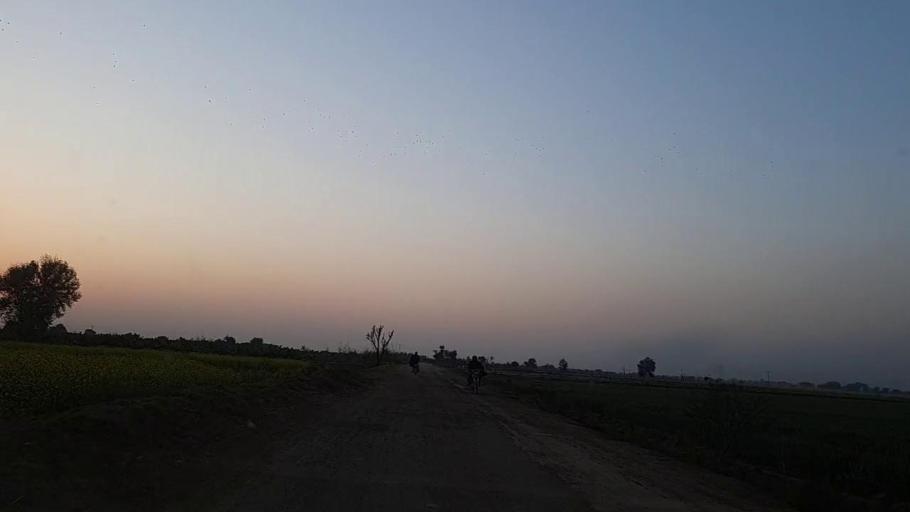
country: PK
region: Sindh
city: Hala
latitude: 25.9444
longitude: 68.4349
